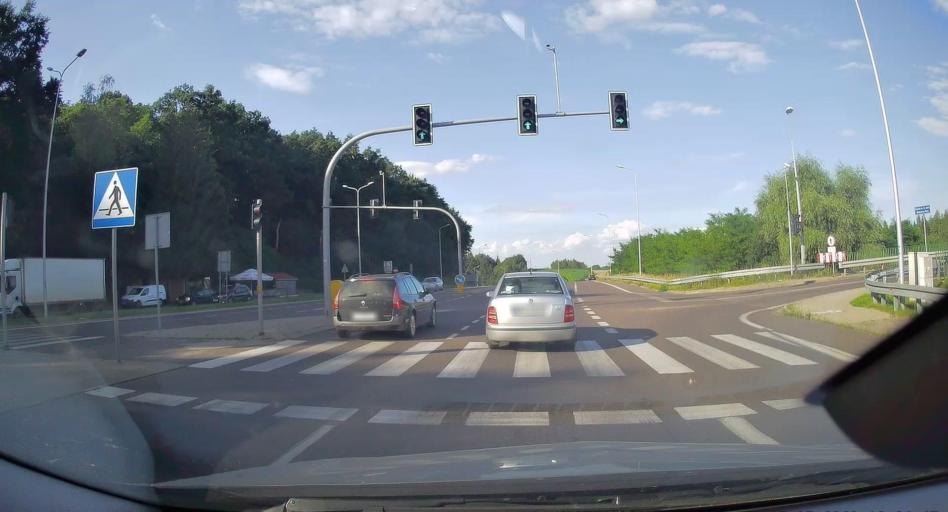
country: PL
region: Subcarpathian Voivodeship
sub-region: Powiat przemyski
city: Zurawica
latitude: 49.8097
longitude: 22.7778
